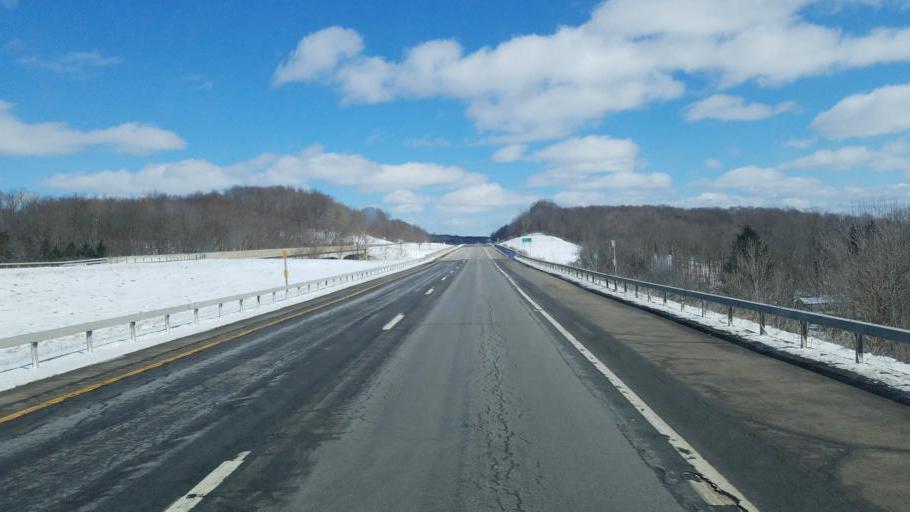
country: US
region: New York
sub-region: Chautauqua County
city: Lakewood
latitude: 42.1281
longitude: -79.3123
